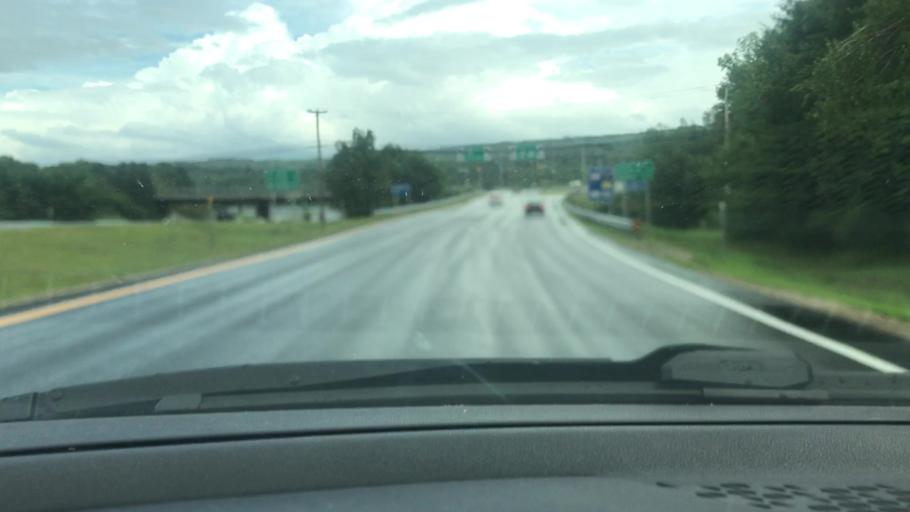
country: US
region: New Hampshire
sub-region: Merrimack County
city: East Concord
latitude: 43.2351
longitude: -71.4734
